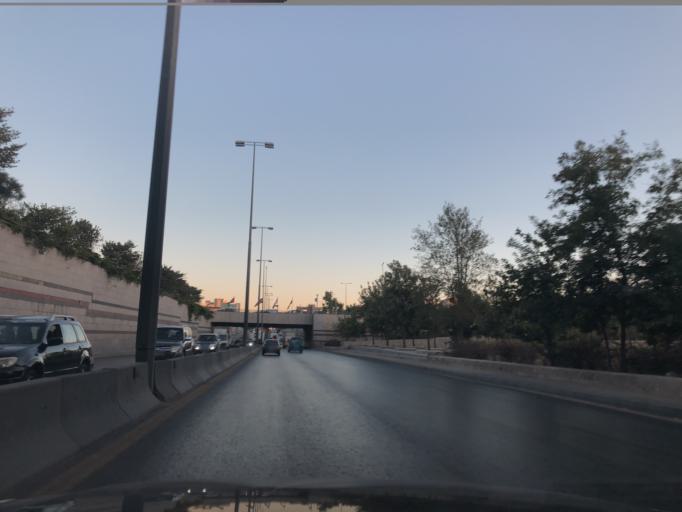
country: JO
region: Amman
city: Wadi as Sir
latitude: 31.9745
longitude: 35.8388
